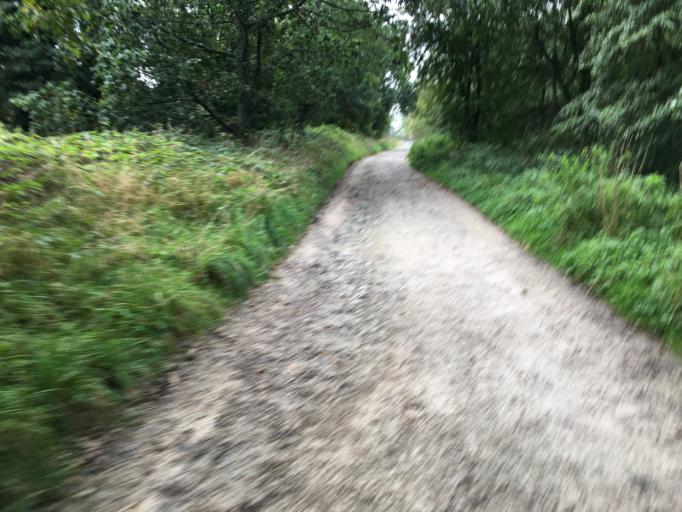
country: GB
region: England
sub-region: North Yorkshire
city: Sleights
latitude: 54.4038
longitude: -0.7235
